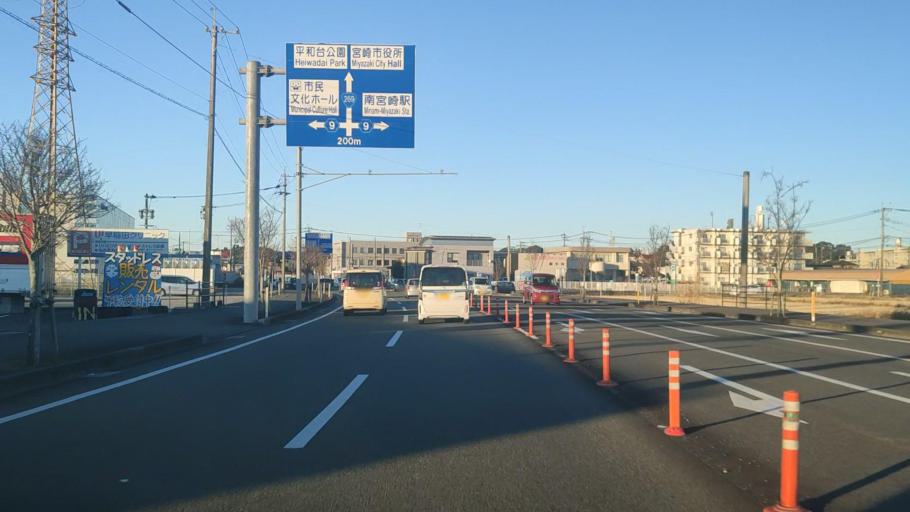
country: JP
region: Miyazaki
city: Miyazaki-shi
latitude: 31.8941
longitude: 131.4068
